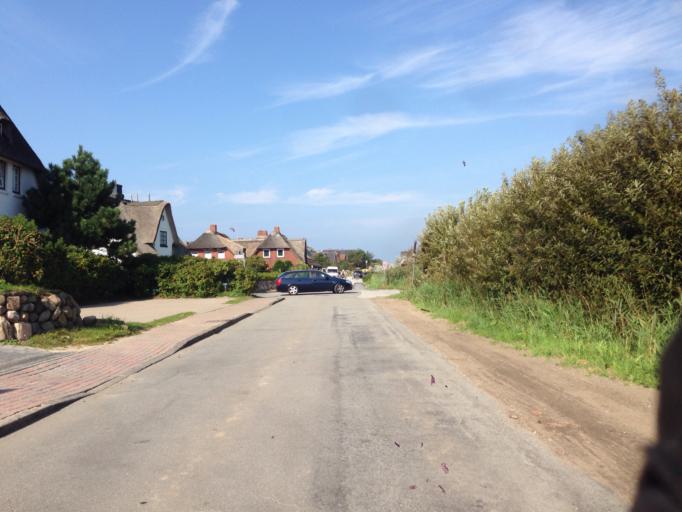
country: DE
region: Schleswig-Holstein
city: Westerland
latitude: 54.8454
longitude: 8.2951
